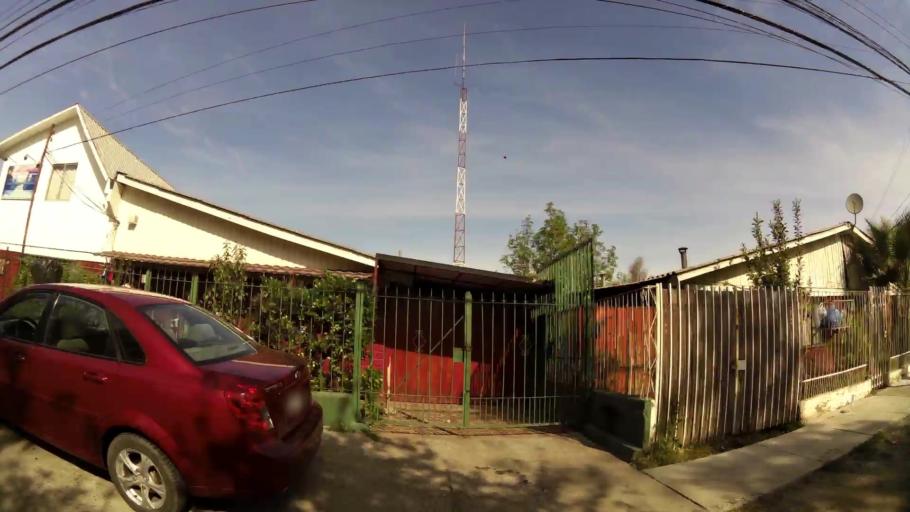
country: CL
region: Santiago Metropolitan
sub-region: Provincia de Santiago
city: Villa Presidente Frei, Nunoa, Santiago, Chile
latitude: -33.5187
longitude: -70.5876
